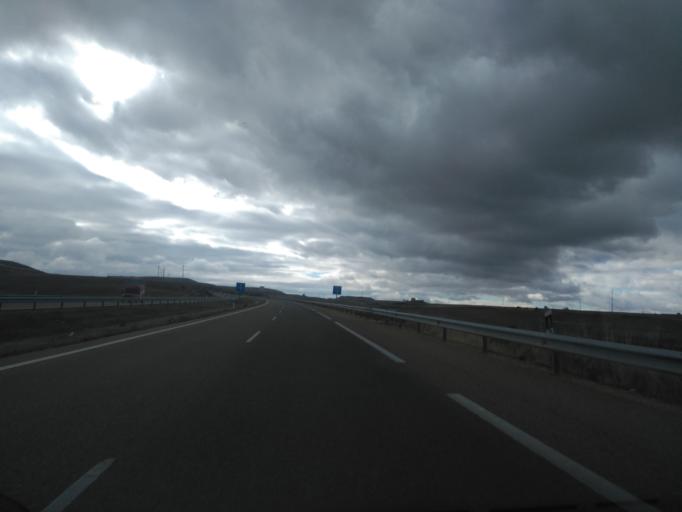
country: ES
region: Castille and Leon
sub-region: Provincia de Palencia
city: Monzon de Campos
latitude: 42.1277
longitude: -4.4775
